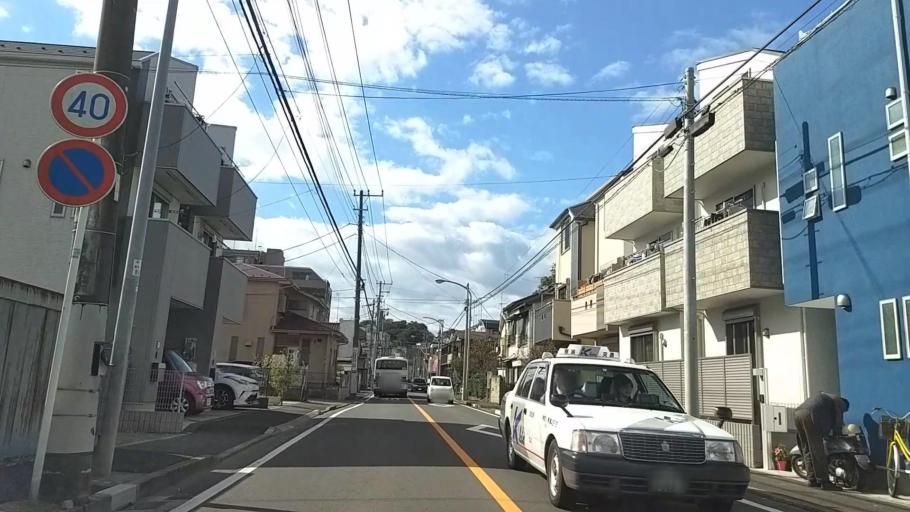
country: JP
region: Kanagawa
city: Yokohama
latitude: 35.5041
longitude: 139.6456
